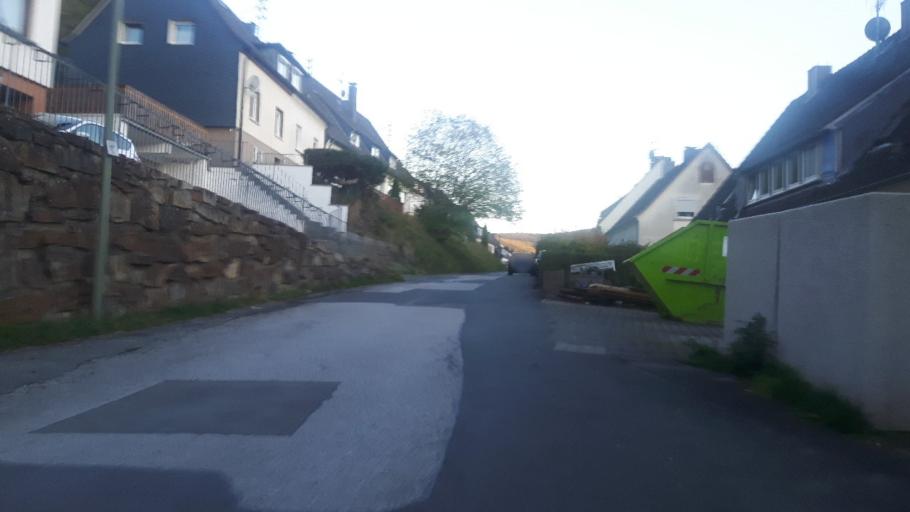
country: DE
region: Rheinland-Pfalz
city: Mudersbach
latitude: 50.8390
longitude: 7.9818
